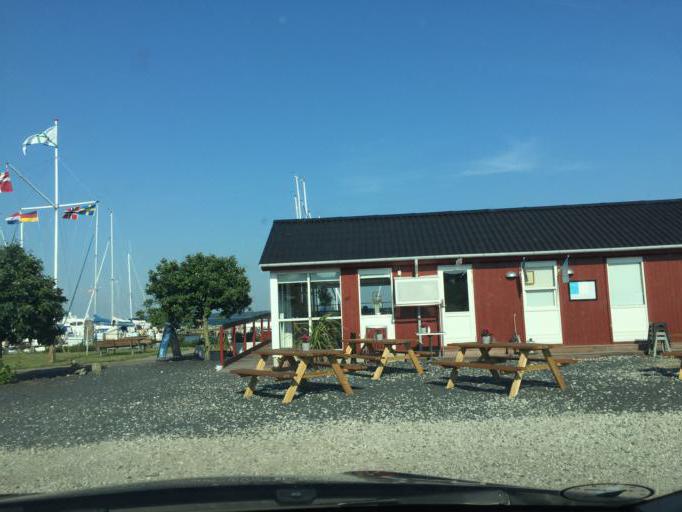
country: DK
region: Zealand
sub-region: Slagelse Kommune
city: Skaelskor
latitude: 55.2105
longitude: 11.1971
